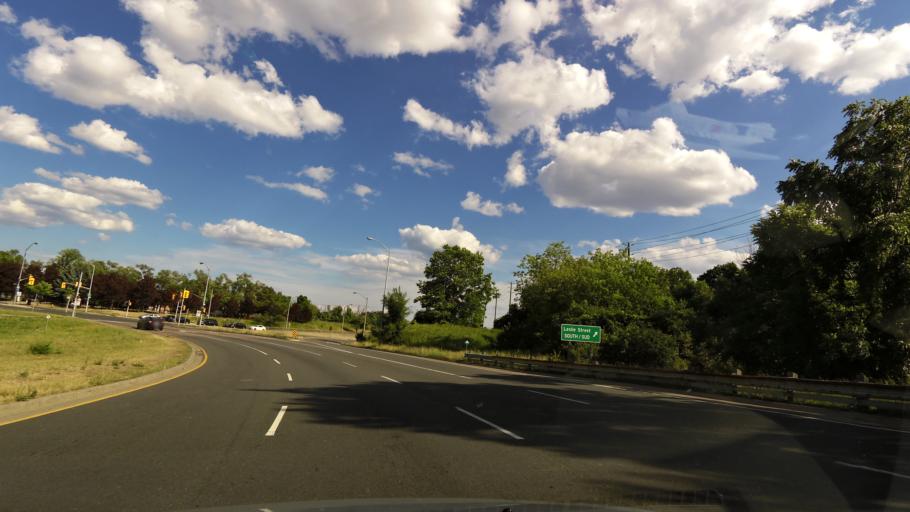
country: CA
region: Ontario
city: Willowdale
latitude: 43.7643
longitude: -79.3630
